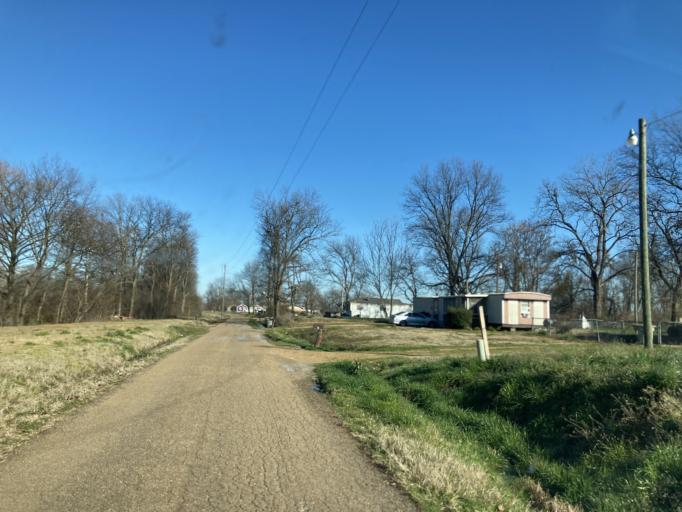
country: US
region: Mississippi
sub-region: Yazoo County
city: Yazoo City
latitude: 32.9529
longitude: -90.5918
